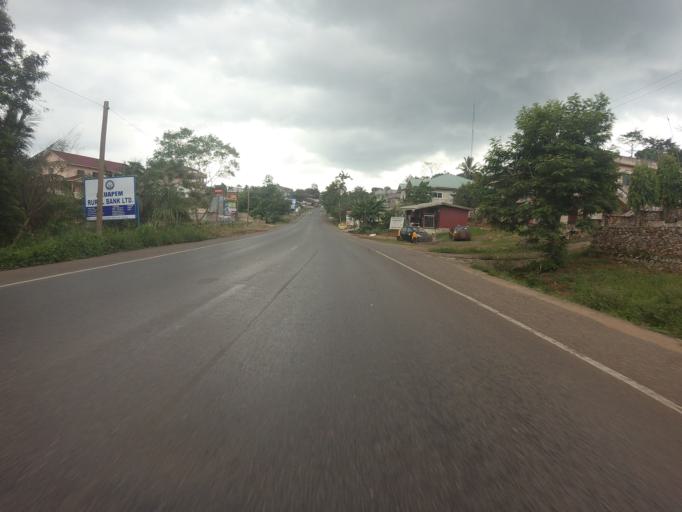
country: GH
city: Akropong
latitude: 5.9376
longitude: -0.1178
